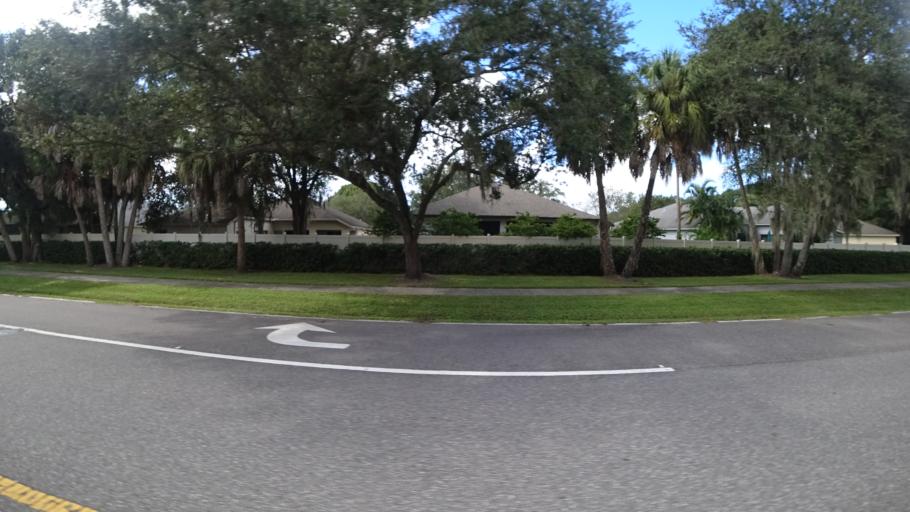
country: US
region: Florida
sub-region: Manatee County
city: Samoset
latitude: 27.4318
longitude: -82.5136
